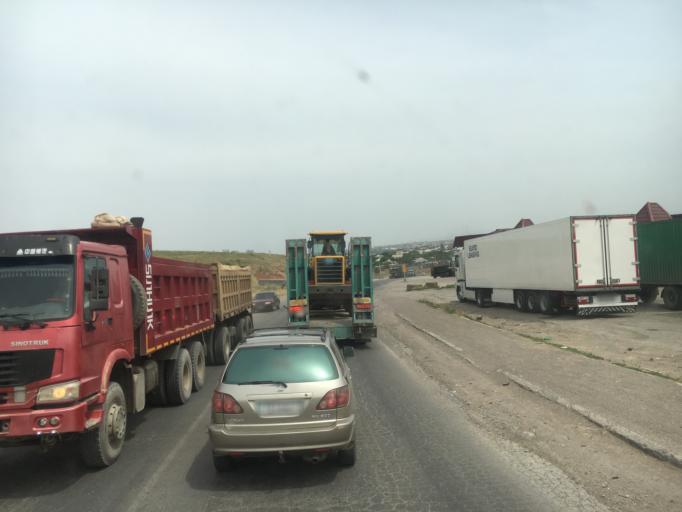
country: KZ
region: Ongtustik Qazaqstan
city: Shymkent
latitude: 42.3289
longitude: 69.5137
